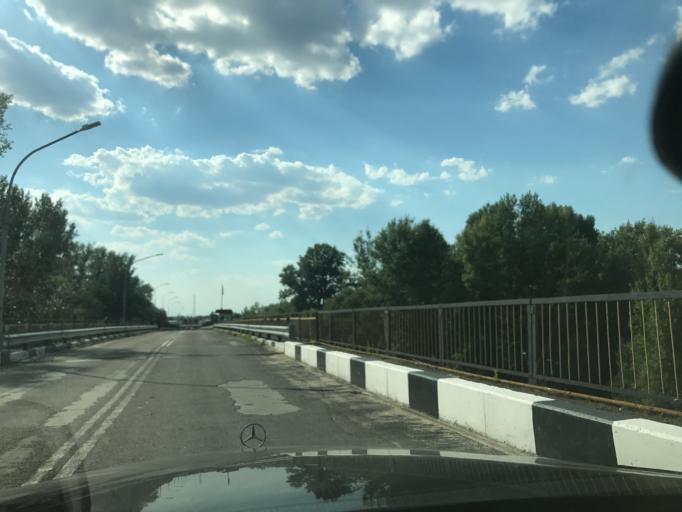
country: PL
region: Lublin Voivodeship
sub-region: Powiat bialski
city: Slawatycze
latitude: 51.7656
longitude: 23.5926
